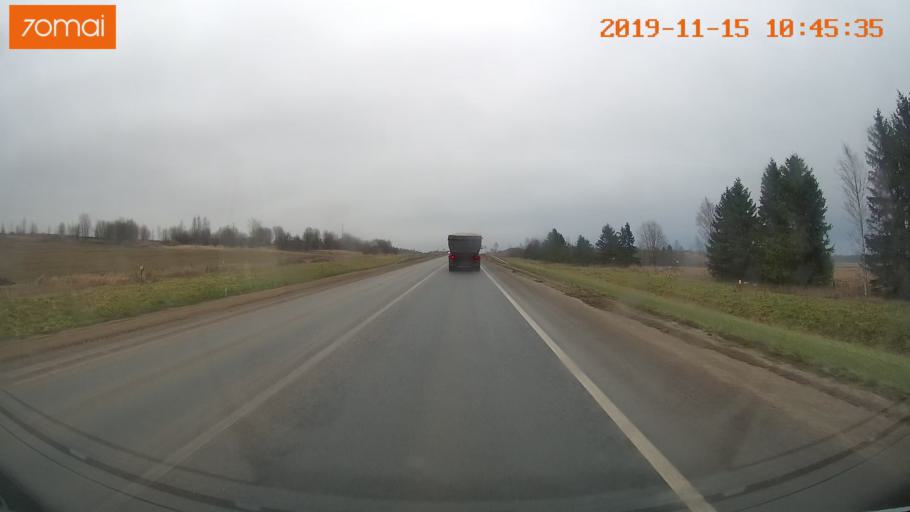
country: RU
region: Vologda
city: Sheksna
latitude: 59.2112
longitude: 38.5908
